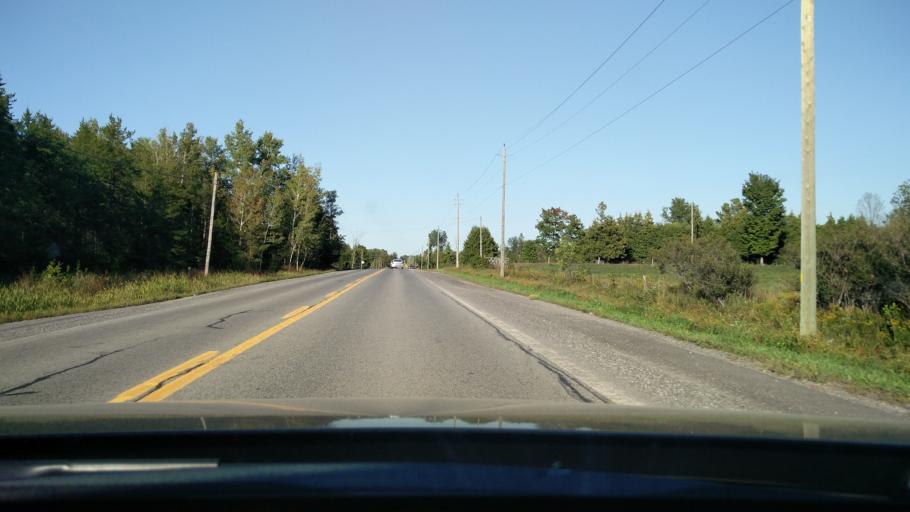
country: CA
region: Ontario
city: Carleton Place
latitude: 45.1162
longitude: -75.9635
